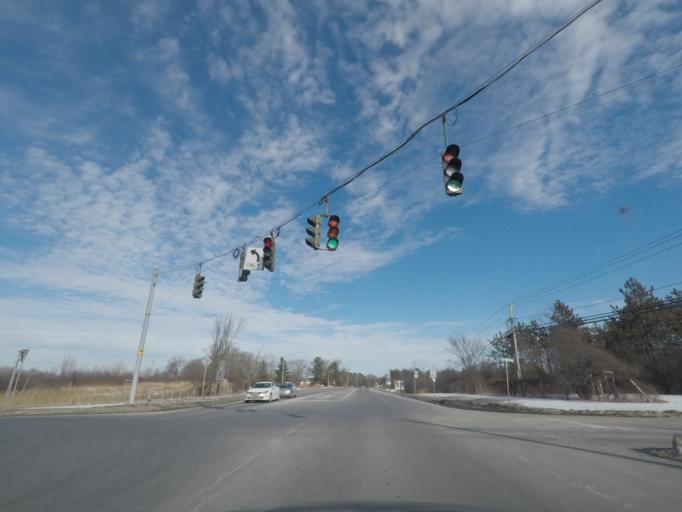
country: US
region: New York
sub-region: Schenectady County
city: Rotterdam
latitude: 42.7817
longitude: -74.0261
